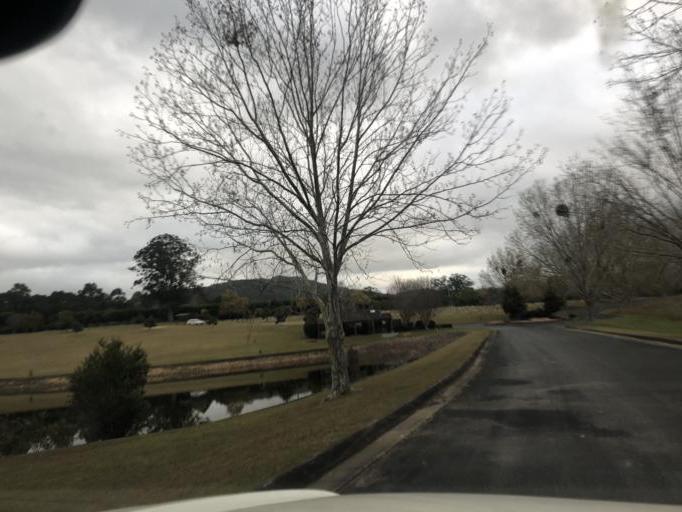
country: AU
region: New South Wales
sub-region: Coffs Harbour
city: Coffs Harbour
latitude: -30.2544
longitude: 153.0530
